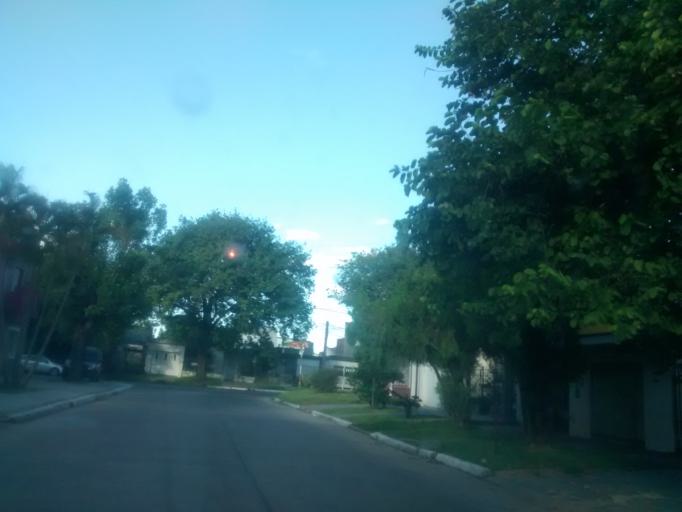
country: AR
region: Chaco
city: Resistencia
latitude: -27.4415
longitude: -58.9792
